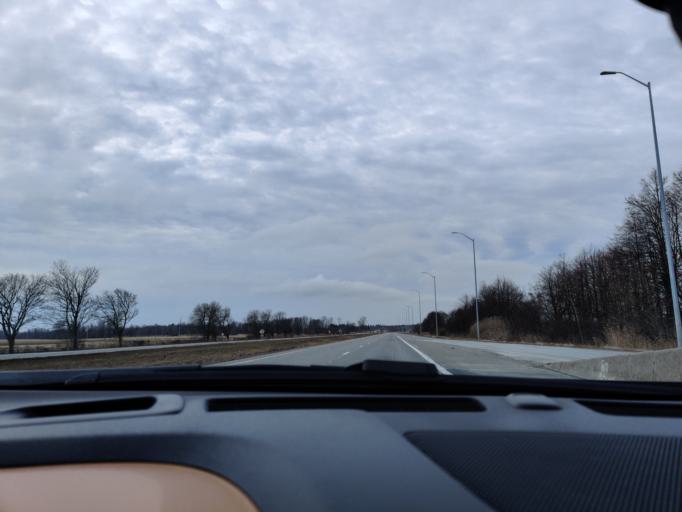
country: CA
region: Ontario
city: Cornwall
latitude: 45.1438
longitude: -74.4869
